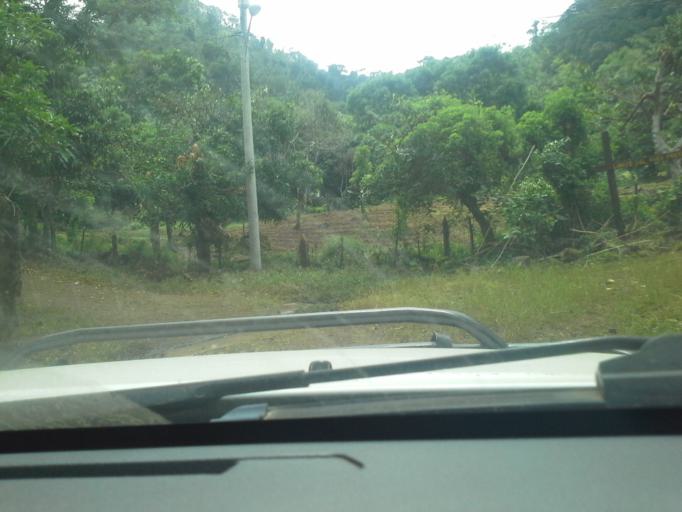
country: NI
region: Boaco
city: San Jose de los Remates
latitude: 12.6933
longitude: -85.7342
